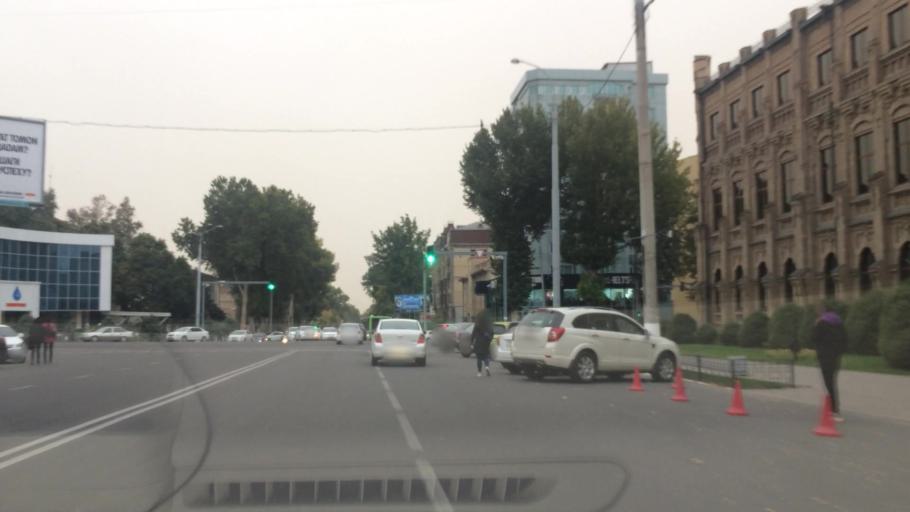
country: UZ
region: Toshkent Shahri
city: Tashkent
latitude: 41.3073
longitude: 69.2836
